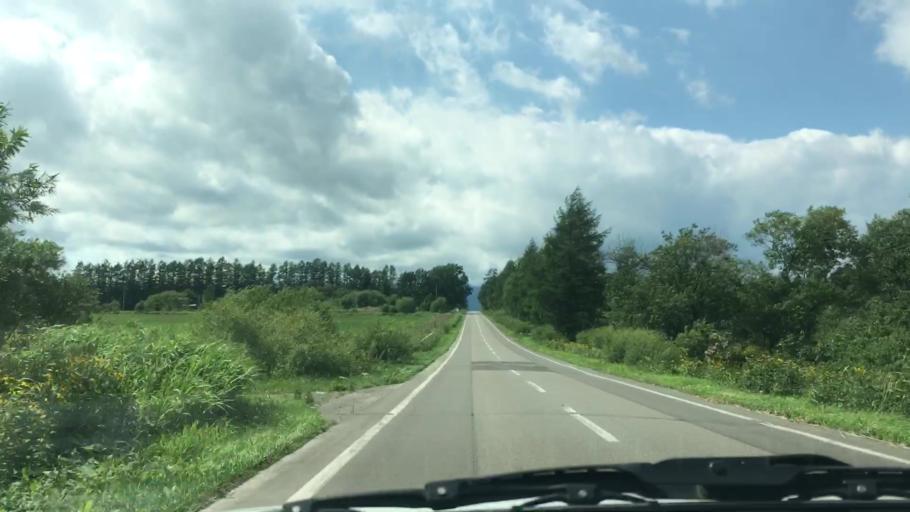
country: JP
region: Hokkaido
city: Otofuke
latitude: 43.2780
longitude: 143.3581
